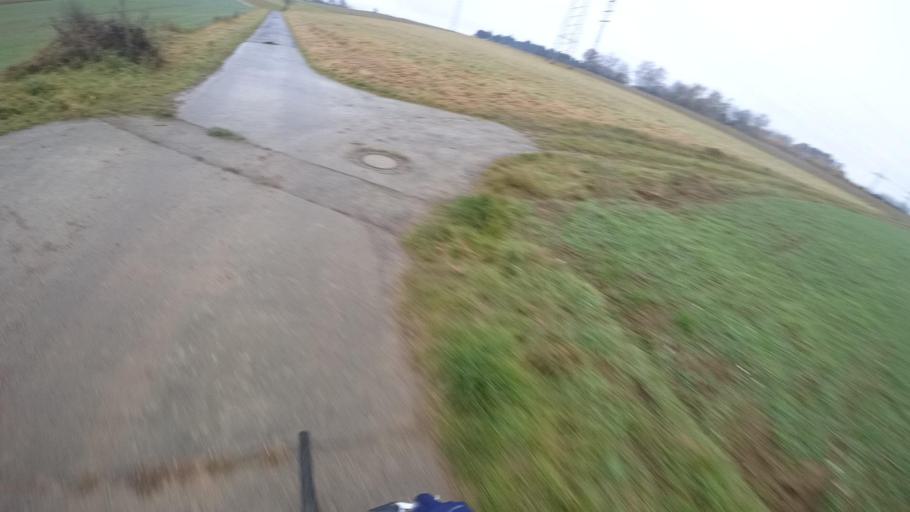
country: DE
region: Rheinland-Pfalz
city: Norath
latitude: 50.1297
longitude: 7.5878
